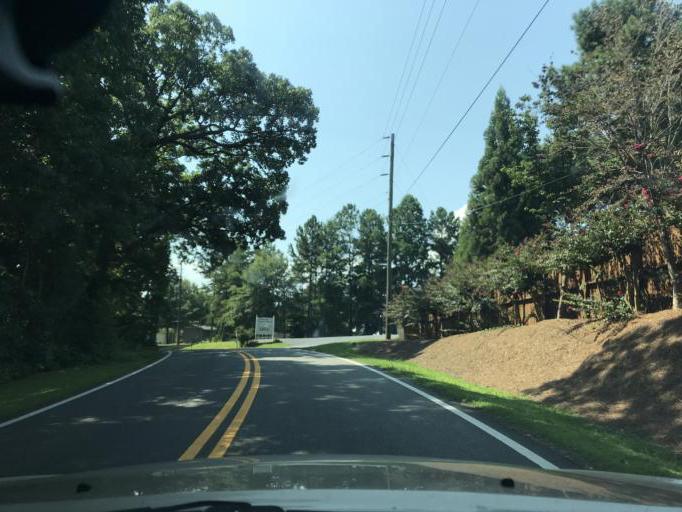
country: US
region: Georgia
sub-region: Hall County
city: Flowery Branch
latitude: 34.2251
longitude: -84.0056
